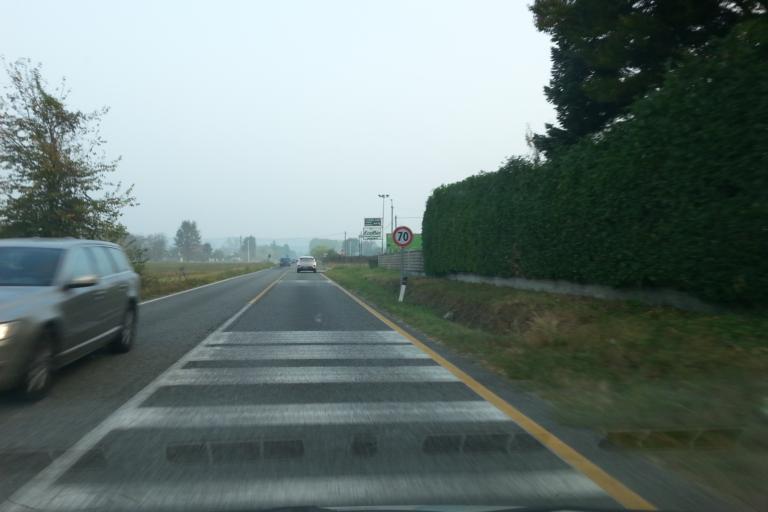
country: IT
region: Piedmont
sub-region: Provincia di Torino
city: Bruino
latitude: 45.0067
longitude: 7.4664
